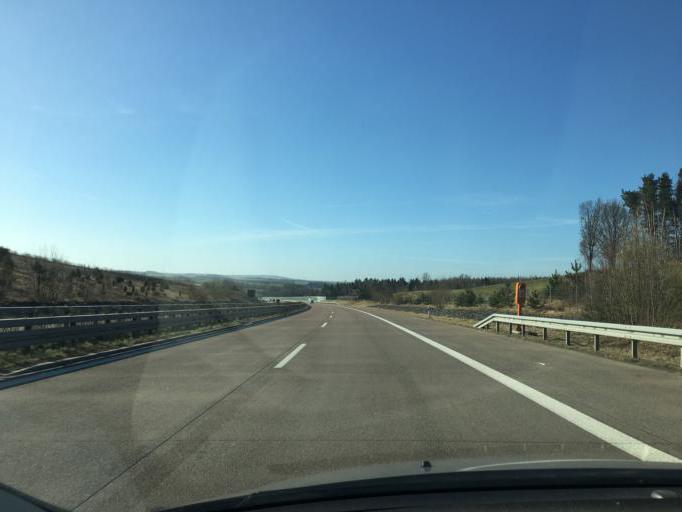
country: DE
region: Saxony
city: Penig
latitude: 50.9370
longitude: 12.6868
